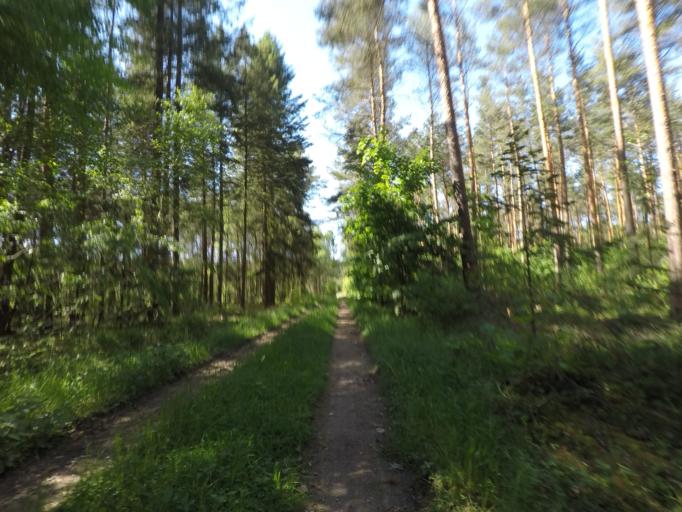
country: DE
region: Brandenburg
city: Melchow
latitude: 52.8233
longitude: 13.7500
